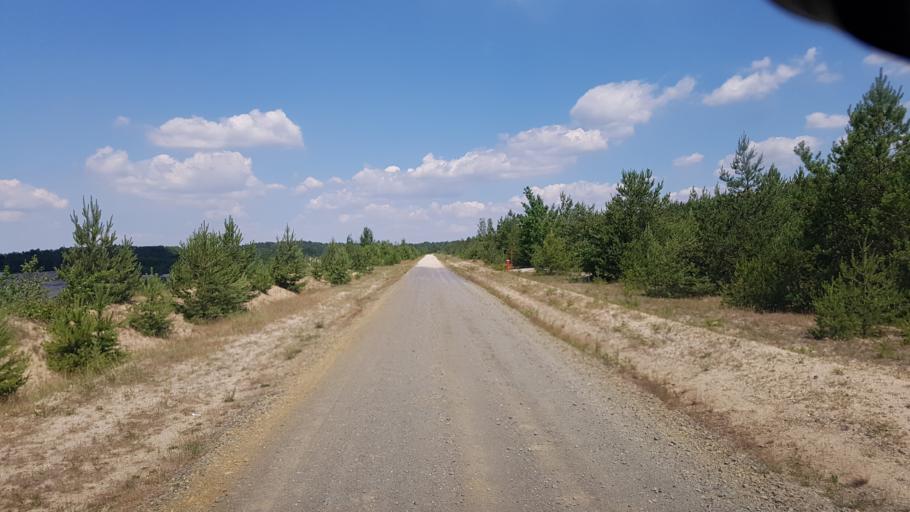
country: DE
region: Brandenburg
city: Sallgast
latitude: 51.5791
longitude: 13.8008
